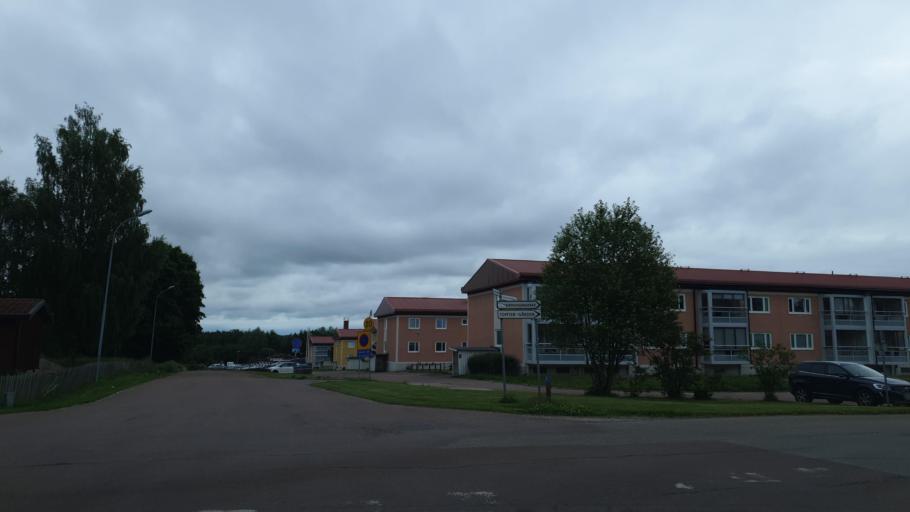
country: SE
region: Dalarna
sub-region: Mora Kommun
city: Mora
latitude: 60.9962
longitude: 14.5432
